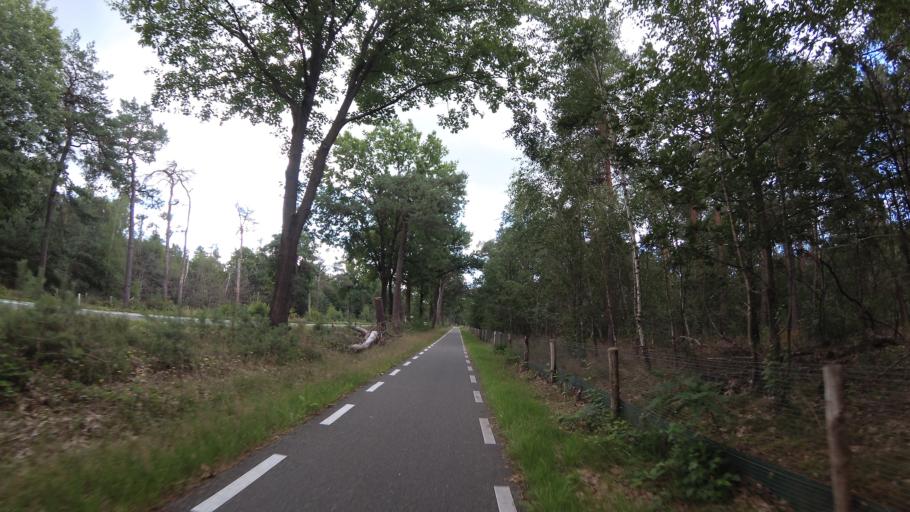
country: NL
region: North Brabant
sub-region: Gemeente Dongen
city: Dongen
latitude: 51.5955
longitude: 4.8978
